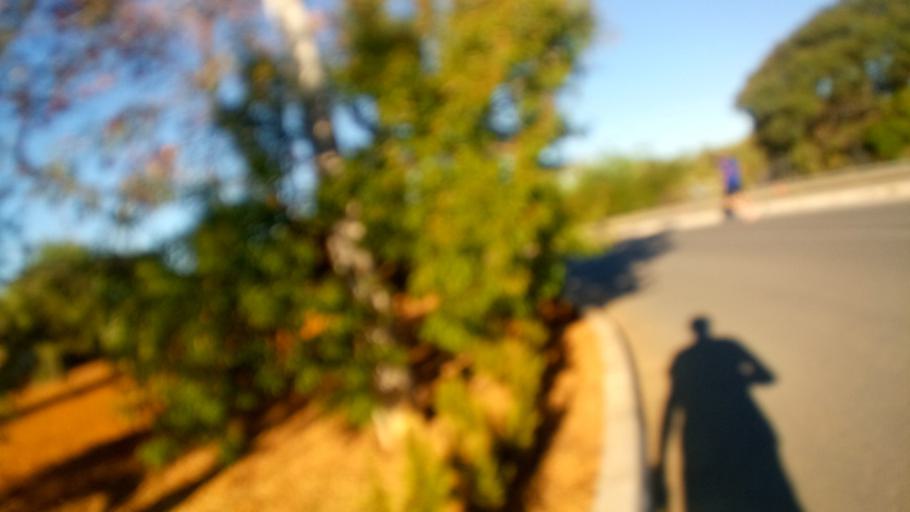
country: PT
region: Faro
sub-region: Tavira
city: Tavira
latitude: 37.1420
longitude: -7.6089
